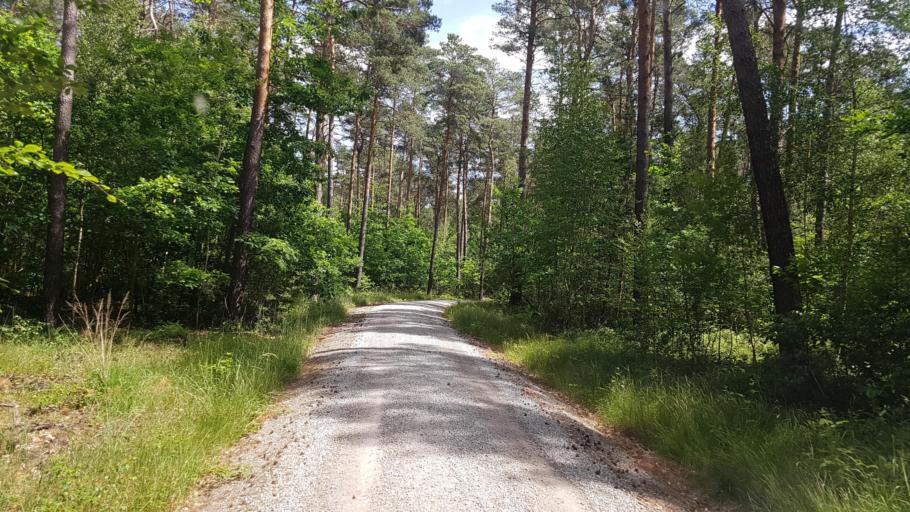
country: DE
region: Brandenburg
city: Plessa
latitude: 51.4953
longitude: 13.6021
